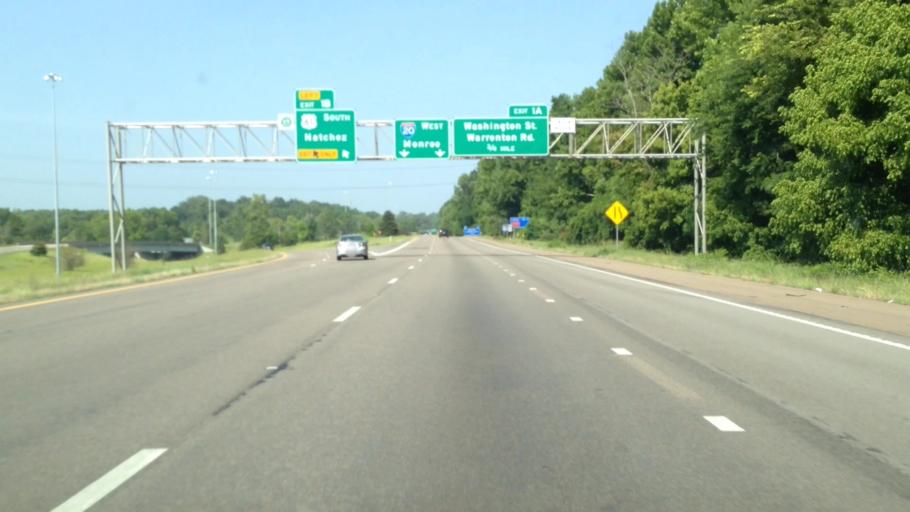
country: US
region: Mississippi
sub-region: Warren County
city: Vicksburg
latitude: 32.3159
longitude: -90.8843
